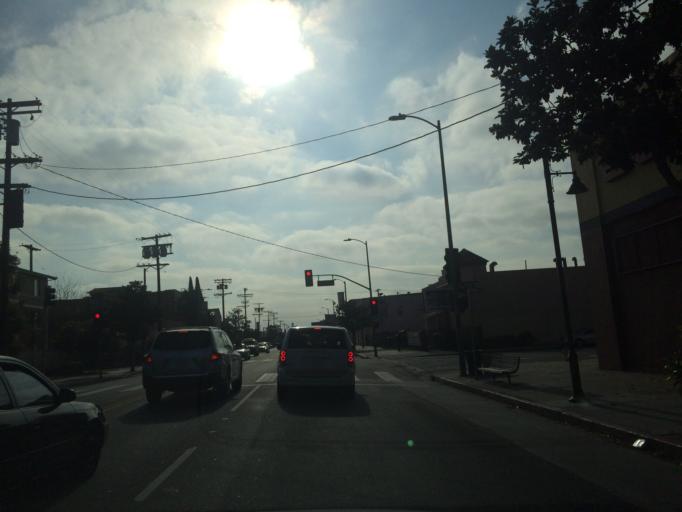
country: US
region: California
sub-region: Los Angeles County
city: View Park-Windsor Hills
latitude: 34.0327
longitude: -118.3032
